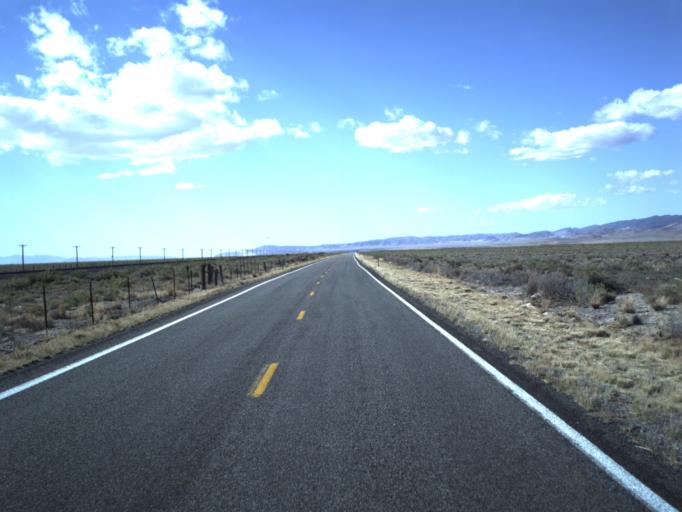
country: US
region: Utah
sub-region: Millard County
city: Delta
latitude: 39.1351
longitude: -112.7286
